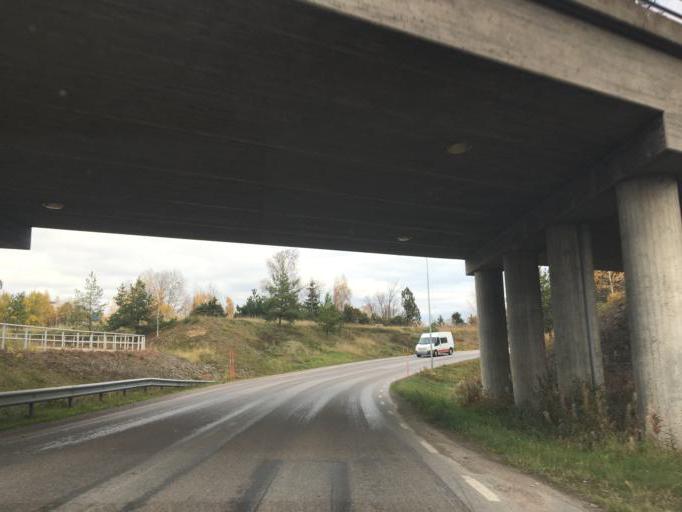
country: SE
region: Vaestmanland
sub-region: Vasteras
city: Skultuna
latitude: 59.5741
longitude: 16.3983
